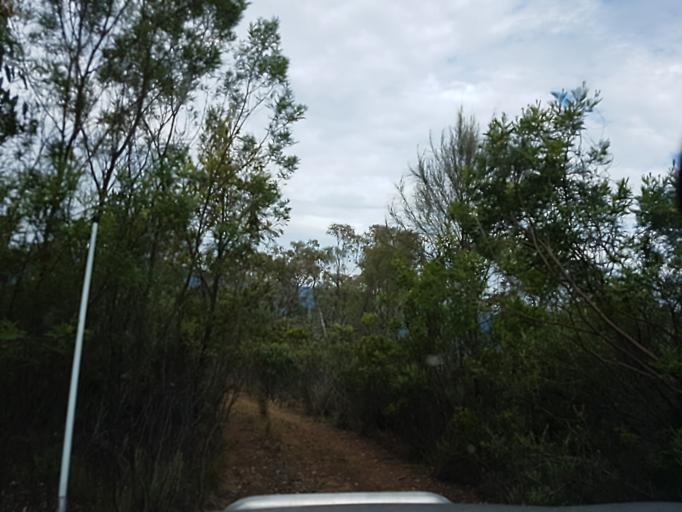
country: AU
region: New South Wales
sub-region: Snowy River
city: Jindabyne
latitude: -36.9999
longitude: 148.4012
